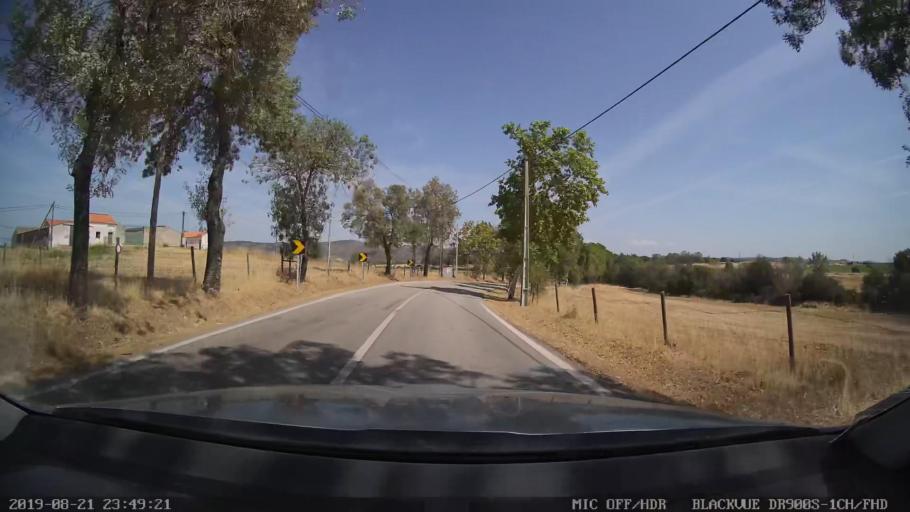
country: PT
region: Castelo Branco
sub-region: Idanha-A-Nova
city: Idanha-a-Nova
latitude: 39.8770
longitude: -7.2511
